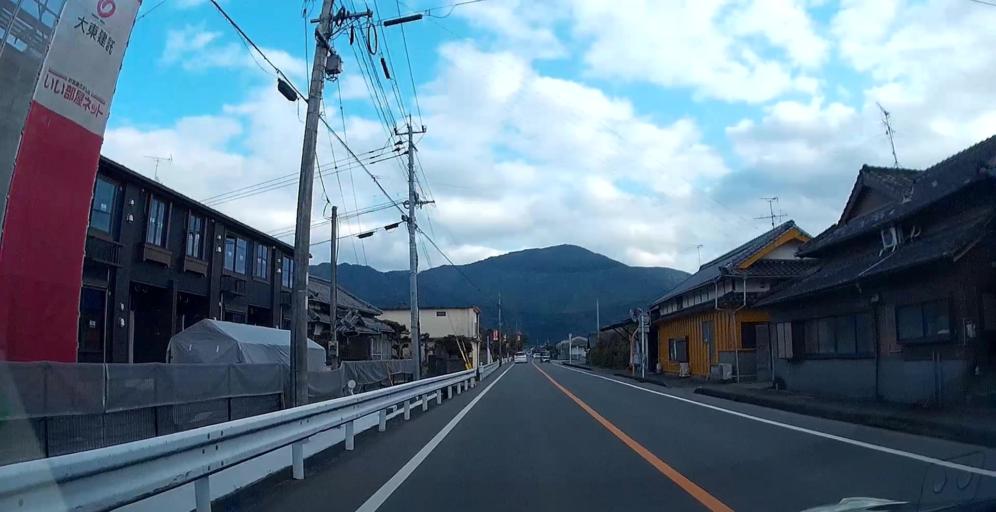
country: JP
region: Kumamoto
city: Yatsushiro
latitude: 32.5340
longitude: 130.6499
